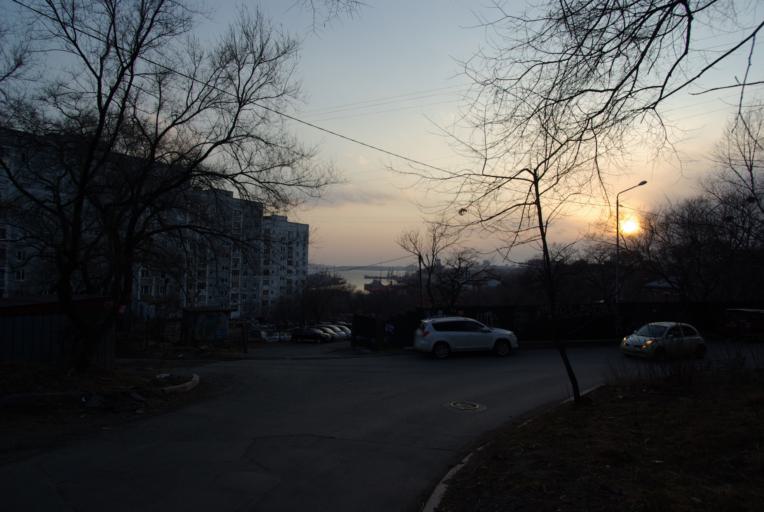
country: RU
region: Primorskiy
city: Vladivostok
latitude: 43.0958
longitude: 131.9063
